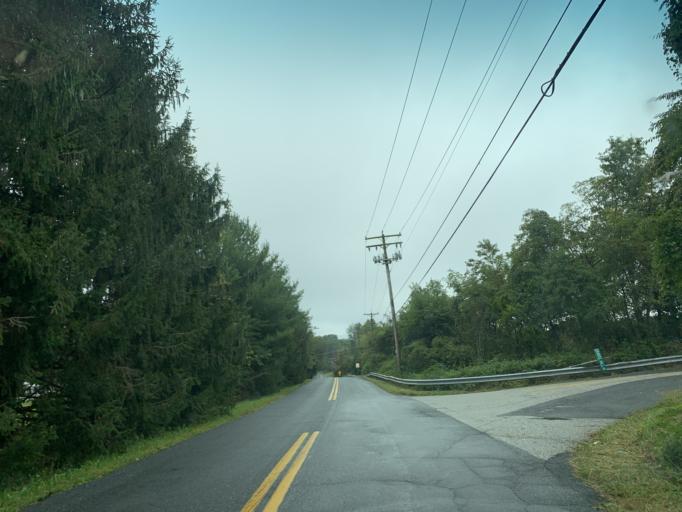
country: US
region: Maryland
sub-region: Harford County
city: Aberdeen
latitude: 39.5673
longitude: -76.1489
